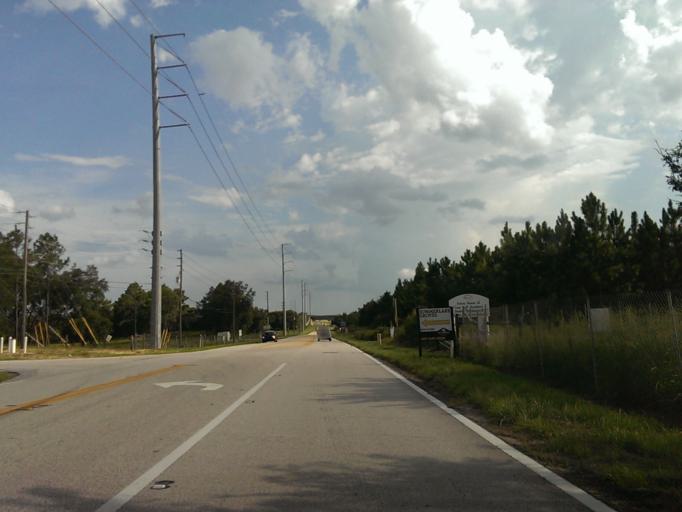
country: US
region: Florida
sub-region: Polk County
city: Citrus Ridge
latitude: 28.4419
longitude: -81.6364
